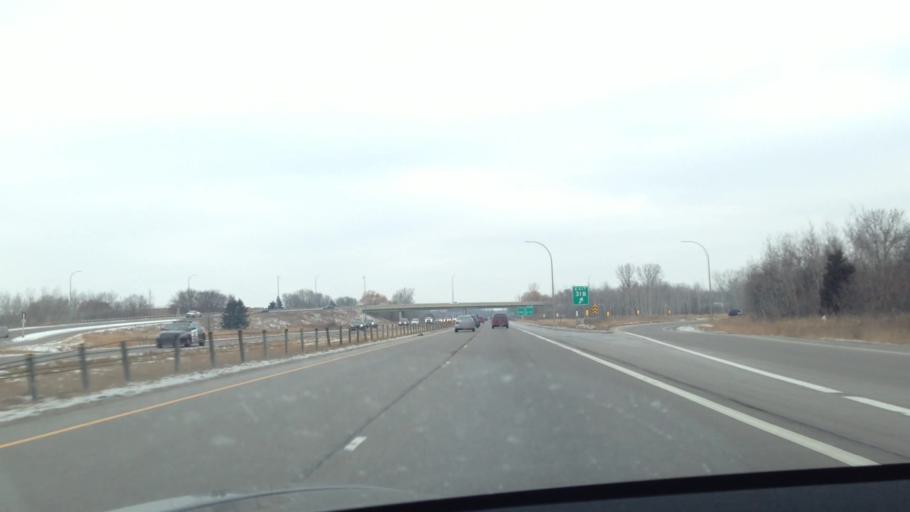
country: US
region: Minnesota
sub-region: Ramsey County
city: Mounds View
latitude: 45.1246
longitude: -93.1884
